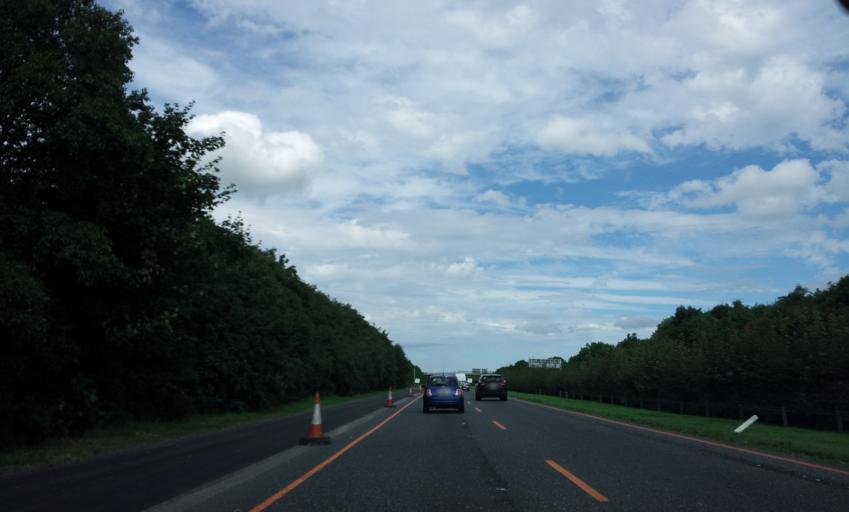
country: IE
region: Leinster
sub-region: Kildare
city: Kilcullen
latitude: 53.1819
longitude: -6.7377
